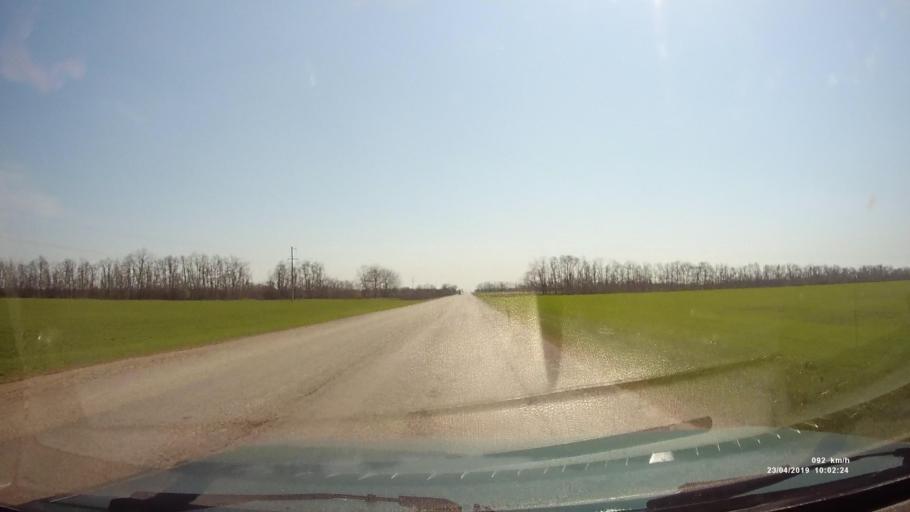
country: RU
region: Rostov
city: Sovetskoye
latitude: 46.7603
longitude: 42.1682
